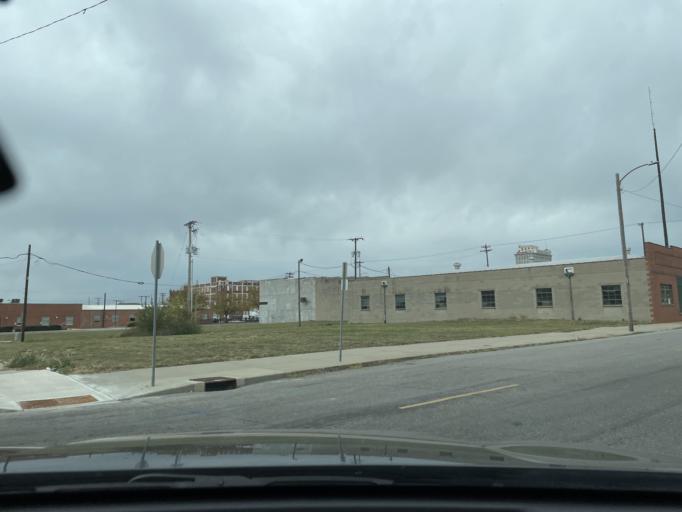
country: US
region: Missouri
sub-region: Buchanan County
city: Saint Joseph
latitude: 39.7626
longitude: -94.8518
